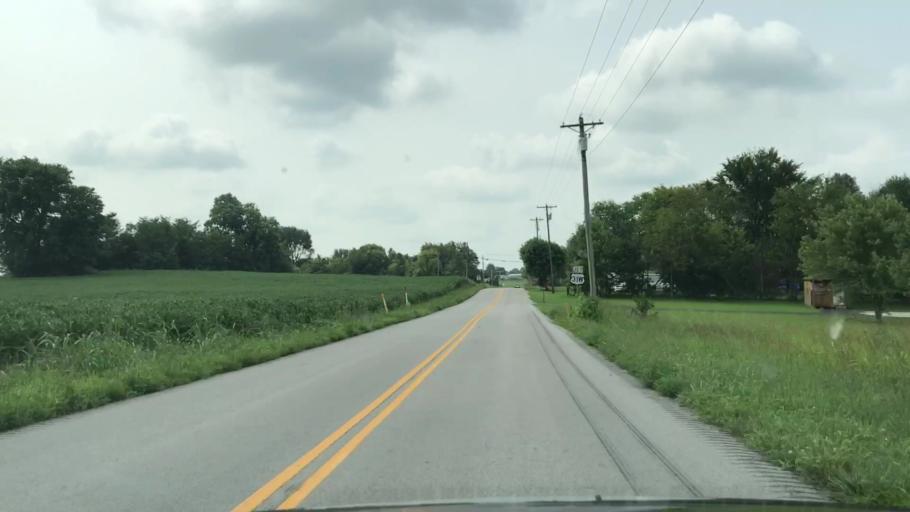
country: US
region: Kentucky
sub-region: Edmonson County
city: Brownsville
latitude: 37.0943
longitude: -86.1476
